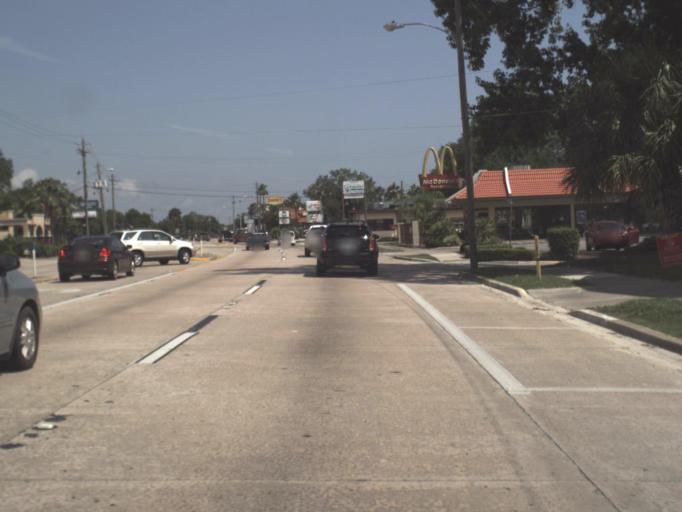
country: US
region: Florida
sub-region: Saint Johns County
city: Saint Augustine
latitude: 29.9021
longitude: -81.3202
